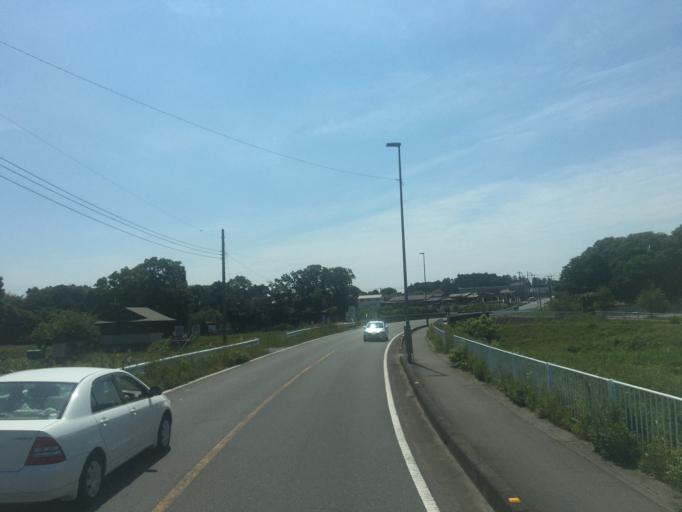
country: JP
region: Saitama
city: Ogawa
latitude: 36.0114
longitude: 139.2998
